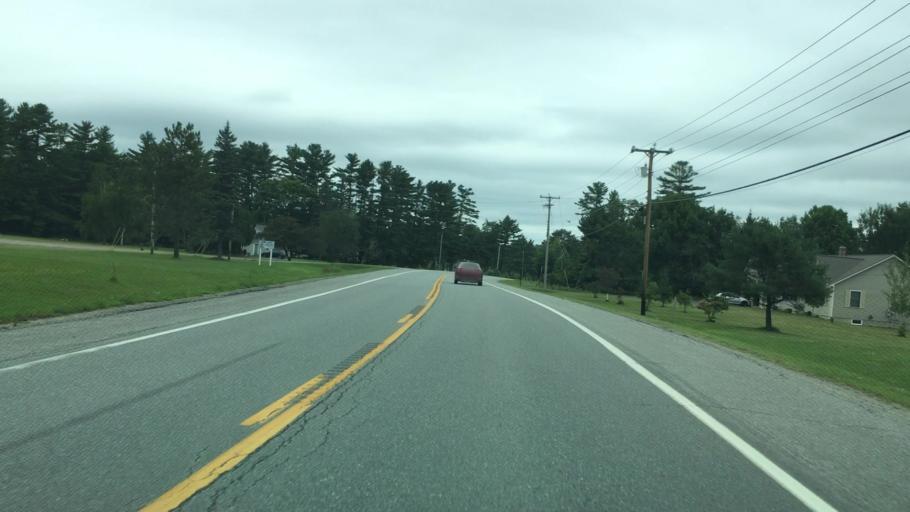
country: US
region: Maine
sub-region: Waldo County
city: Frankfort
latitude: 44.6192
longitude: -68.8700
